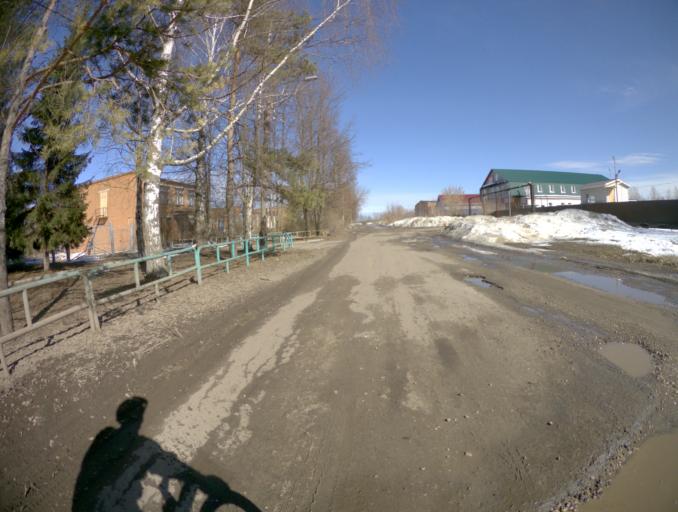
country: RU
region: Vladimir
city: Suzdal'
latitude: 56.4446
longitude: 40.4553
